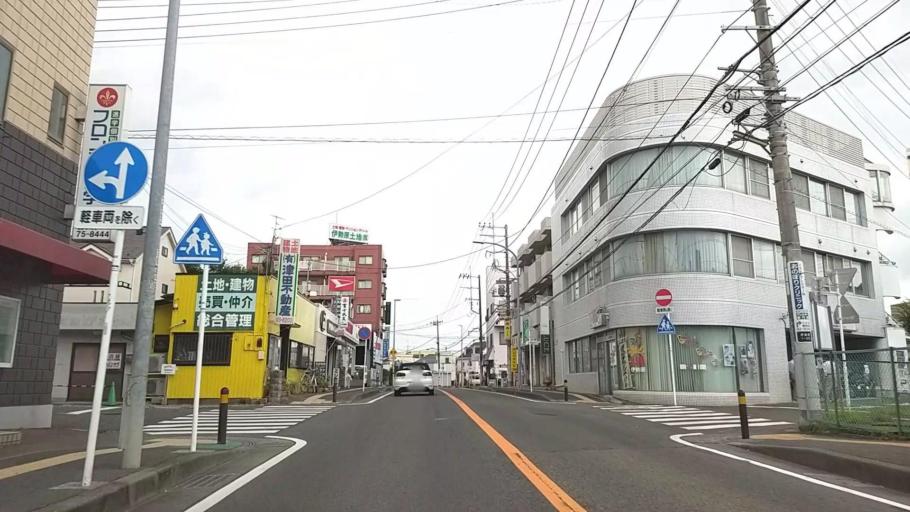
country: JP
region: Kanagawa
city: Isehara
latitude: 35.3975
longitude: 139.3150
